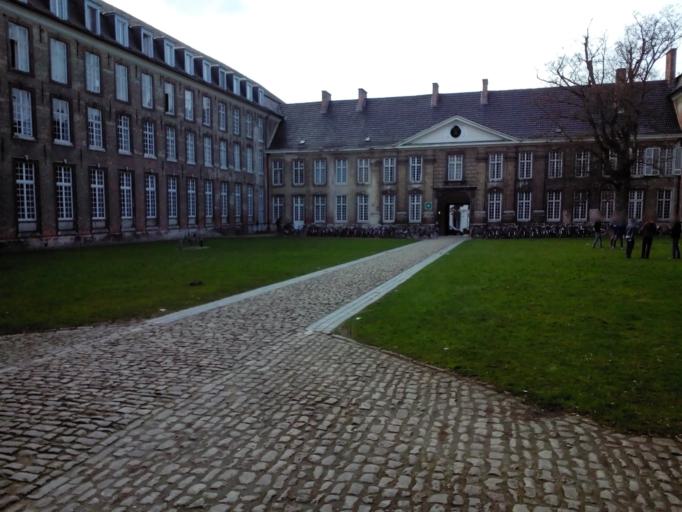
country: BE
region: Flanders
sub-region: Provincie Vlaams-Brabant
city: Leuven
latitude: 50.8771
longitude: 4.7029
